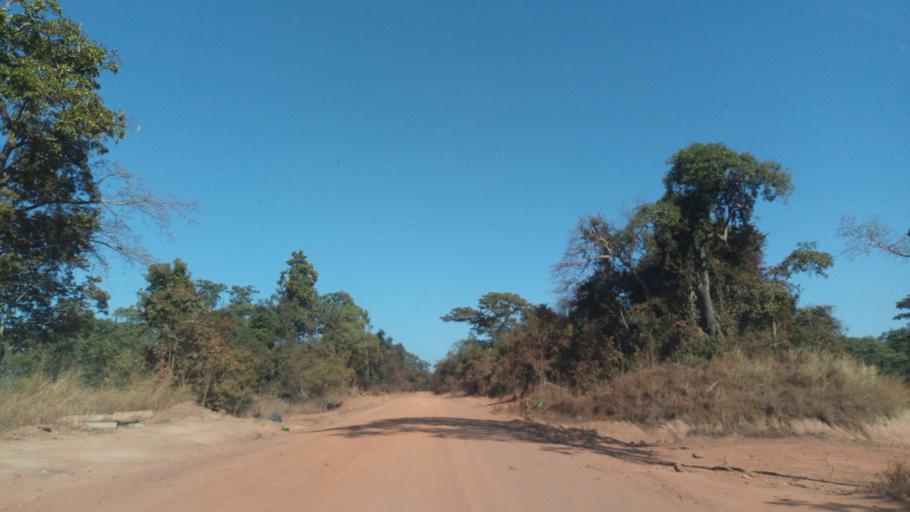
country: ZM
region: Luapula
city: Mwense
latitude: -10.7301
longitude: 28.3551
